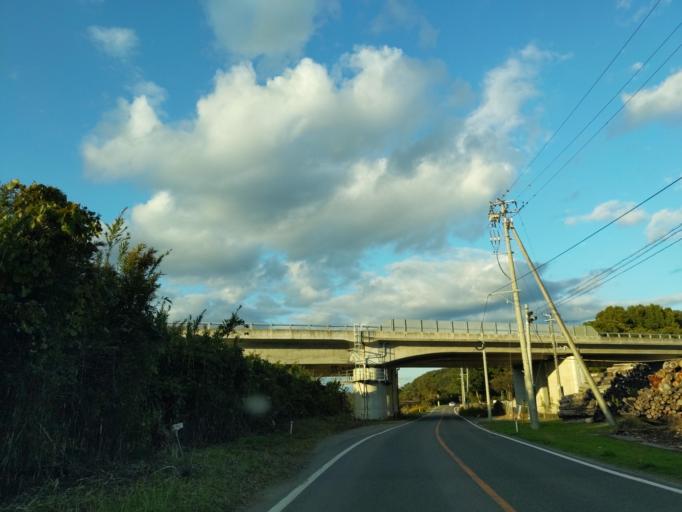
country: JP
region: Fukushima
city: Koriyama
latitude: 37.4422
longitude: 140.4240
